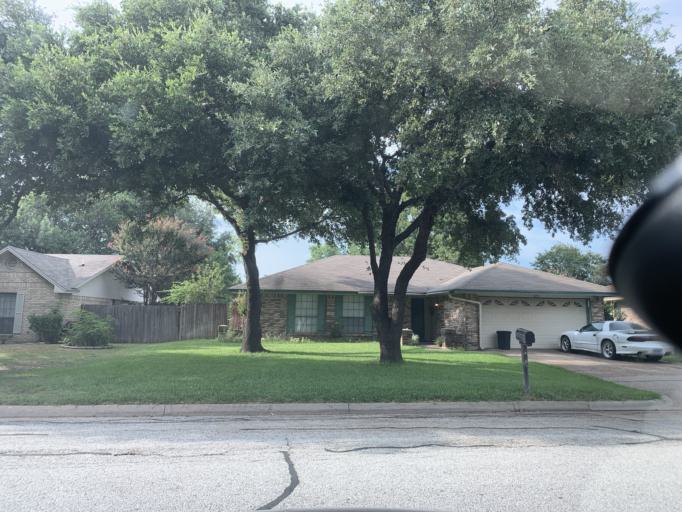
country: US
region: Texas
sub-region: Tarrant County
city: Watauga
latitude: 32.8781
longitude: -97.2364
